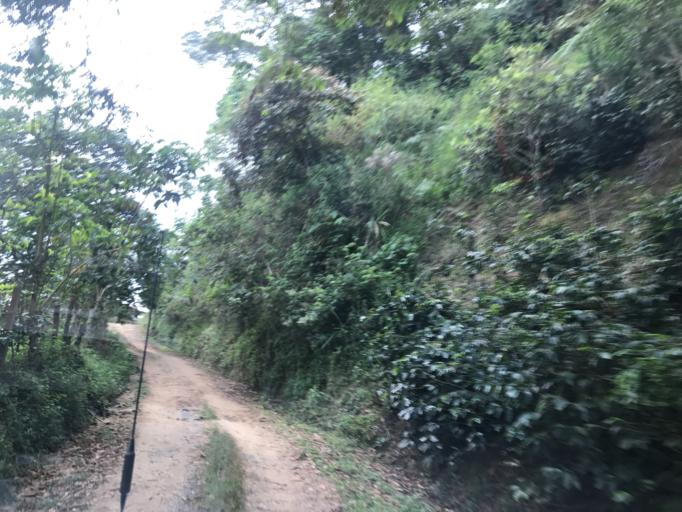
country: CO
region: Valle del Cauca
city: Obando
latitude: 4.5596
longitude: -75.8940
